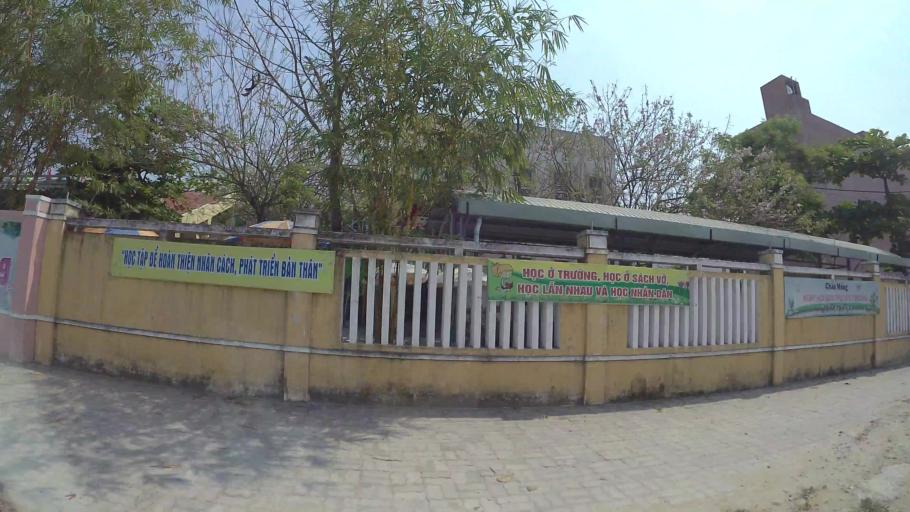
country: VN
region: Da Nang
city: Ngu Hanh Son
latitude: 16.0258
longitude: 108.2474
